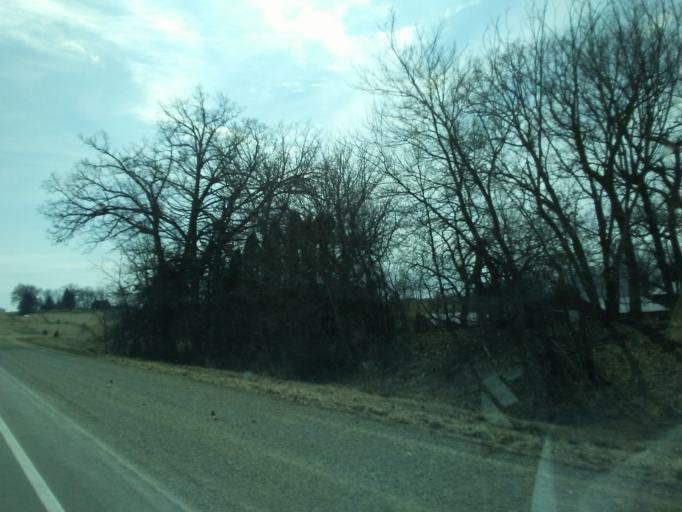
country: US
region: Iowa
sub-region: Winneshiek County
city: Decorah
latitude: 43.4274
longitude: -91.8594
